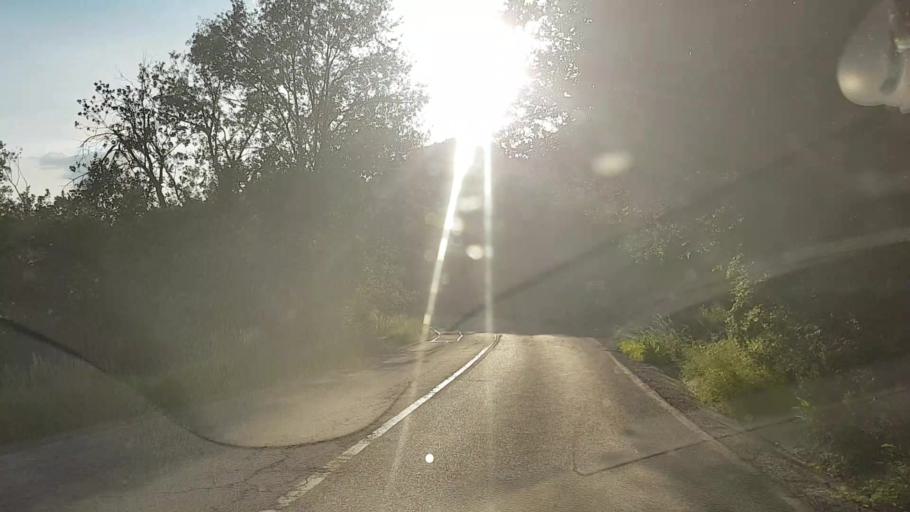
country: RO
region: Harghita
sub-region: Comuna Praid
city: Ocna de Sus
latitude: 46.5729
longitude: 25.2073
